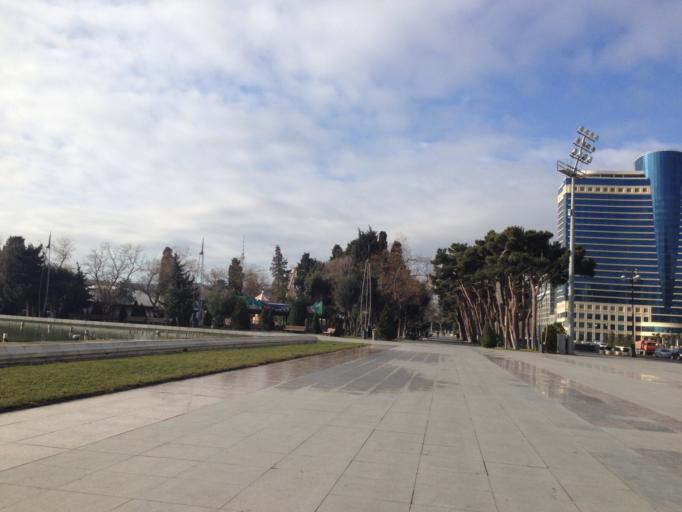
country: AZ
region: Baki
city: Baku
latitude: 40.3725
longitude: 49.8536
